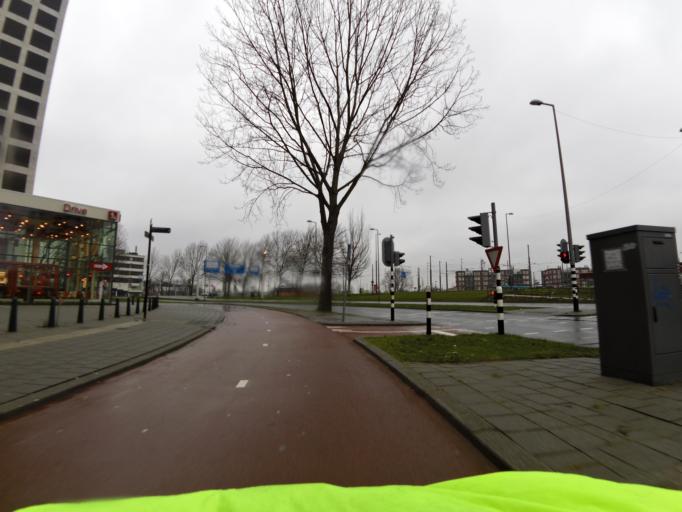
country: NL
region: South Holland
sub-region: Gemeente Rotterdam
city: Delfshaven
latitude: 51.9123
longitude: 4.4326
